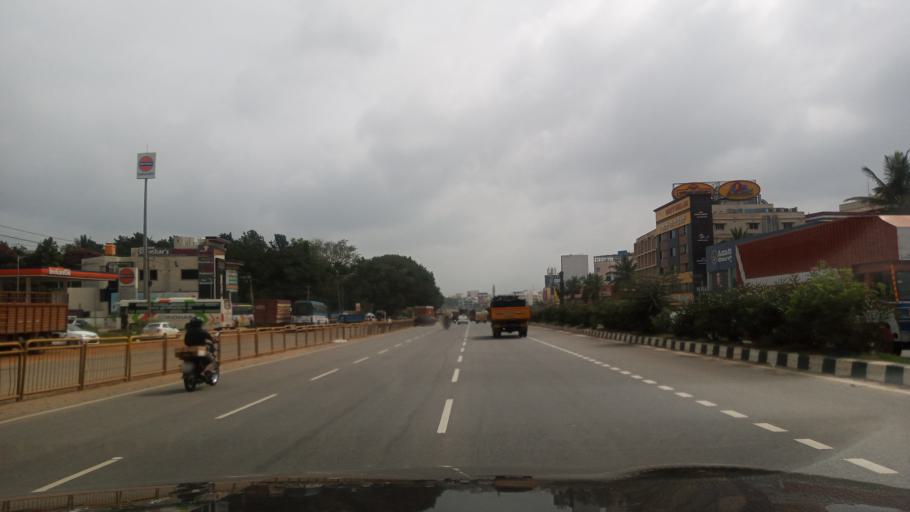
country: IN
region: Karnataka
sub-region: Bangalore Urban
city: Anekal
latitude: 12.8088
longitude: 77.6972
